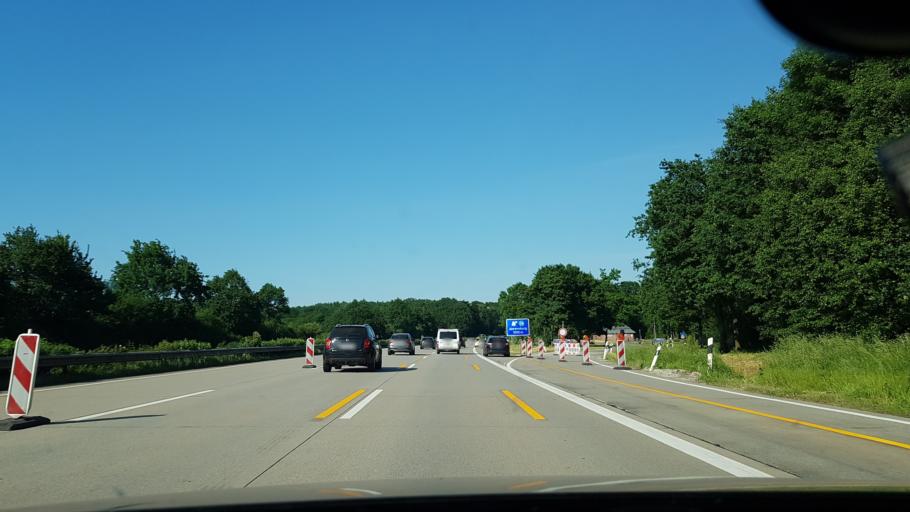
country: DE
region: Schleswig-Holstein
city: Braak
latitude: 53.6355
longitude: 10.2582
